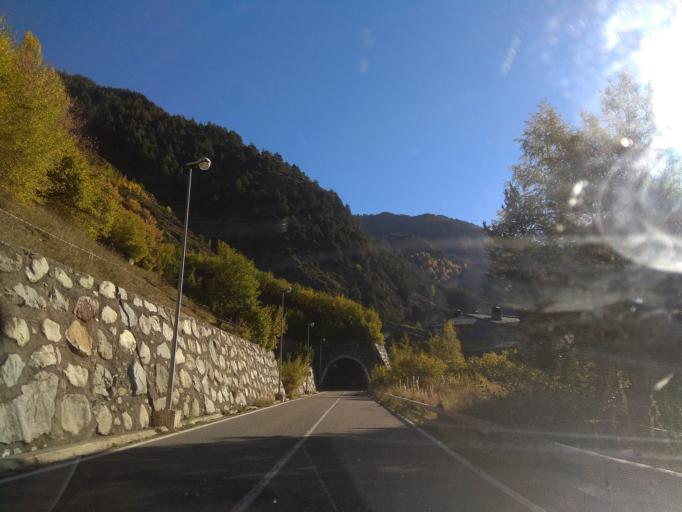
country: AD
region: La Massana
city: Arinsal
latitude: 42.5803
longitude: 1.4770
